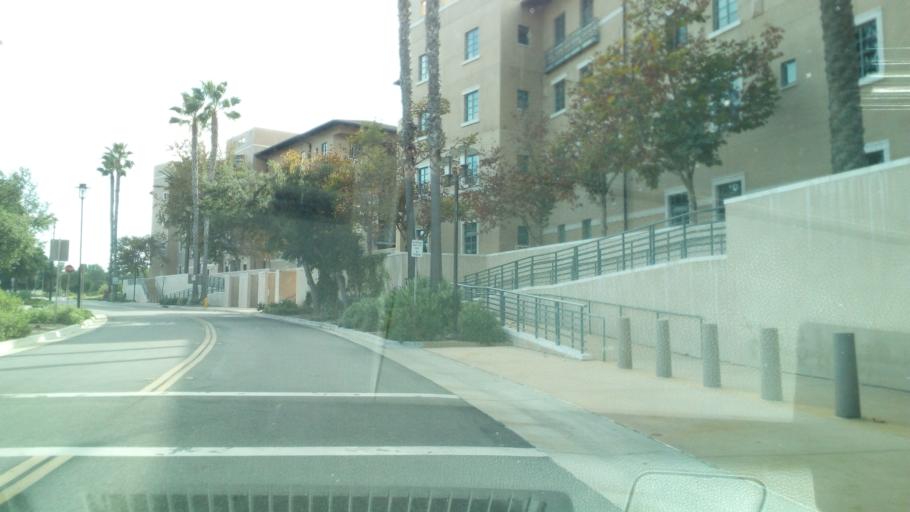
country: US
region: California
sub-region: Orange County
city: Aliso Viejo
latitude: 33.5534
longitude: -117.7354
